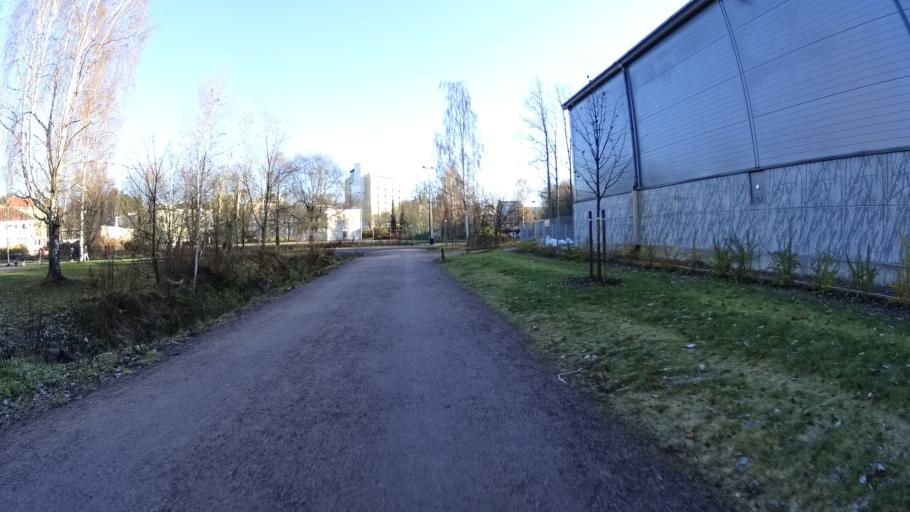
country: FI
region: Uusimaa
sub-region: Helsinki
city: Kilo
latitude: 60.2242
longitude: 24.8074
